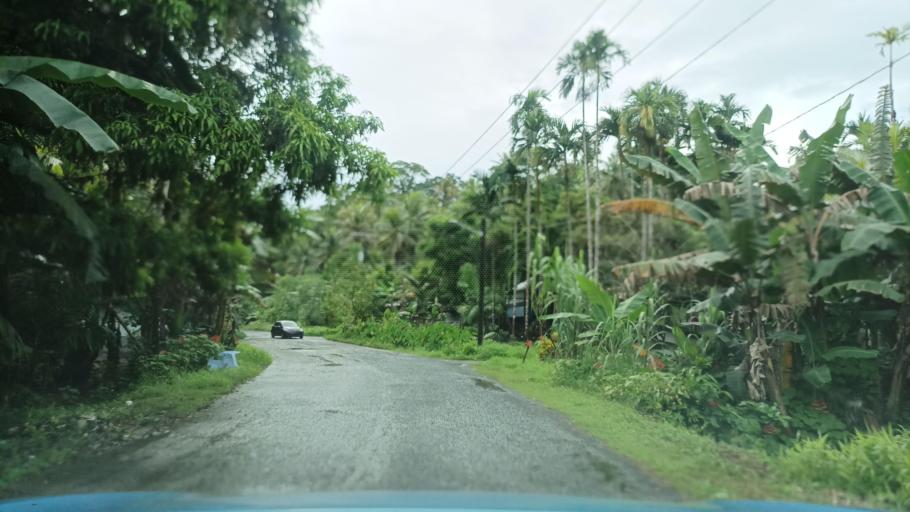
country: FM
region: Pohnpei
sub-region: Sokehs Municipality
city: Palikir - National Government Center
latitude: 6.8221
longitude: 158.1617
